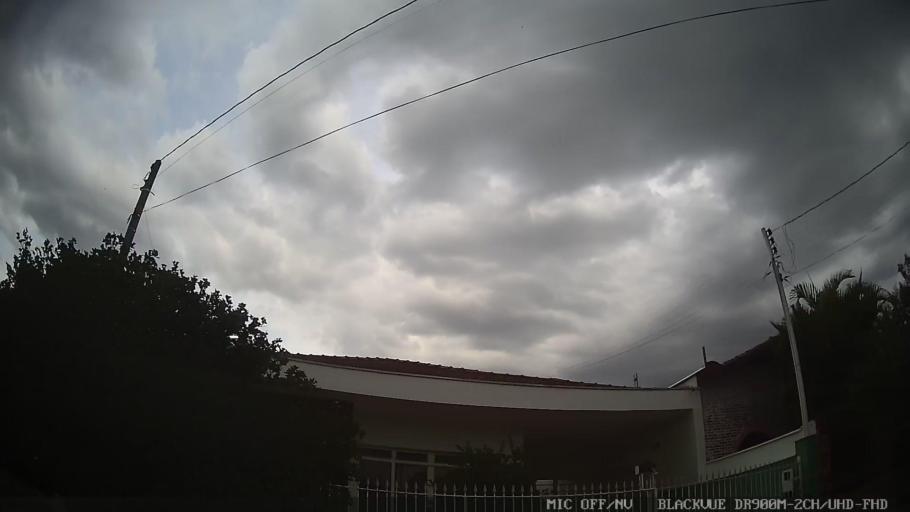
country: BR
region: Sao Paulo
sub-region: Amparo
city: Amparo
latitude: -22.7021
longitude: -46.7534
